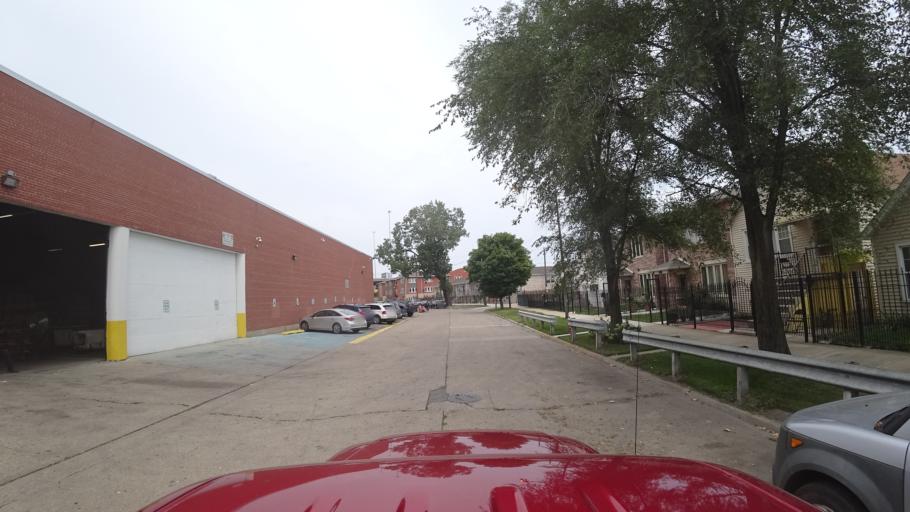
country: US
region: Illinois
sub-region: Cook County
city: Chicago
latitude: 41.8327
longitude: -87.6864
